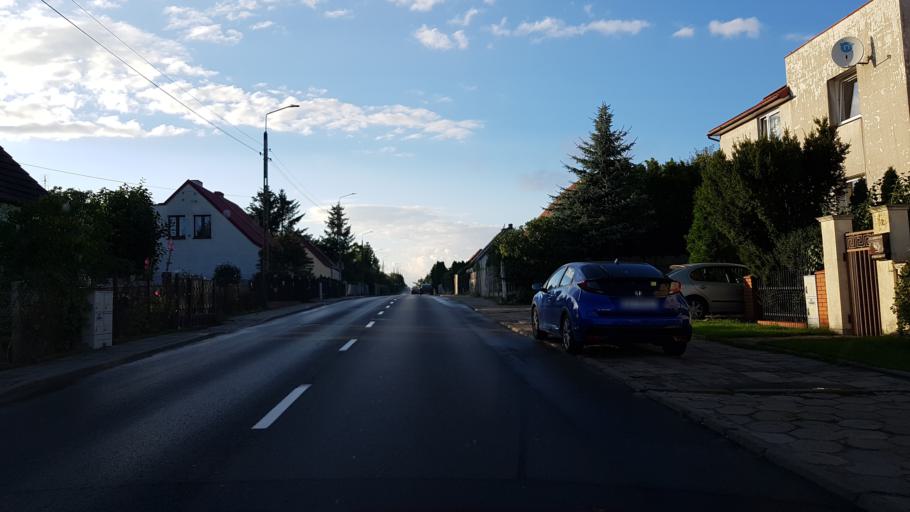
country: PL
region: West Pomeranian Voivodeship
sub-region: Koszalin
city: Koszalin
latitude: 54.2033
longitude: 16.1660
